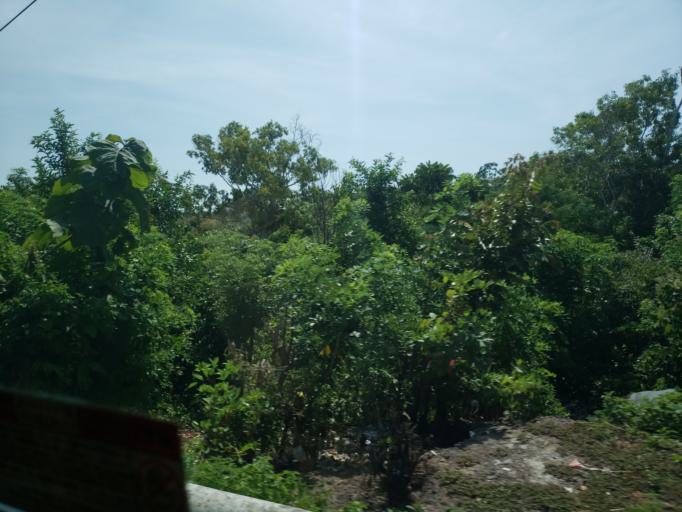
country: ID
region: Bali
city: Kangin
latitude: -8.8345
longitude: 115.1493
